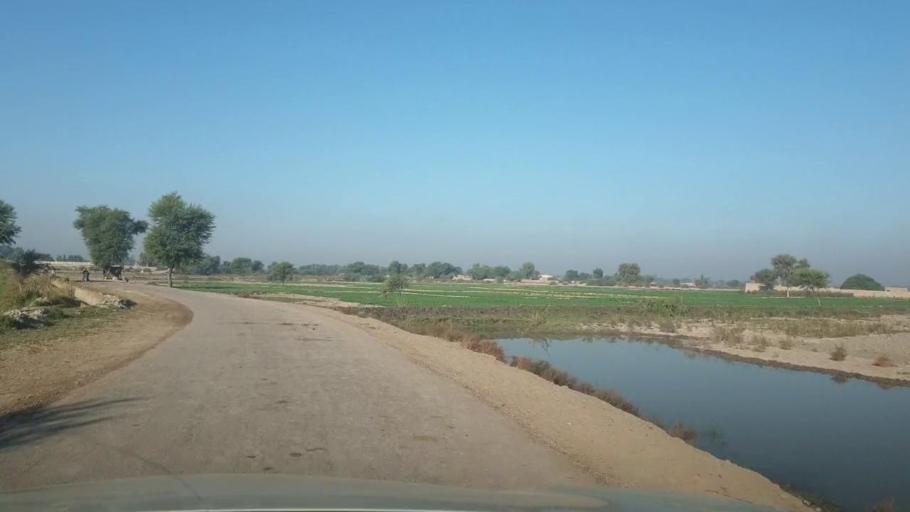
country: PK
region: Sindh
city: Bhan
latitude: 26.5534
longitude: 67.6917
